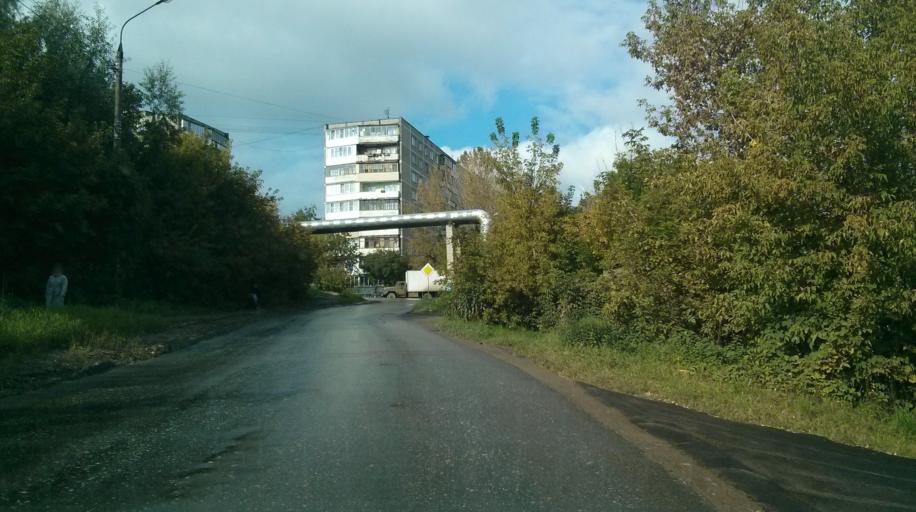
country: RU
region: Nizjnij Novgorod
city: Bor
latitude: 56.3147
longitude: 44.0552
